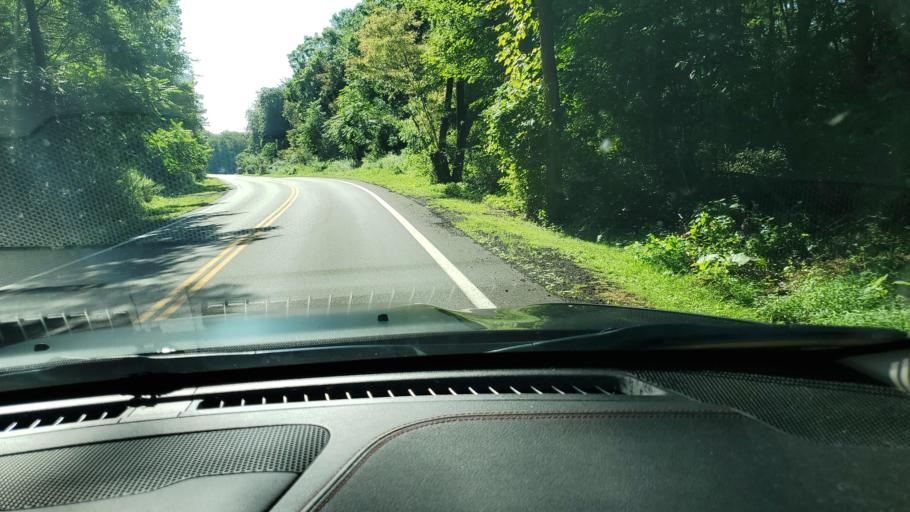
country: US
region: Ohio
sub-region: Mahoning County
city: Lowellville
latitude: 41.0337
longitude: -80.5251
